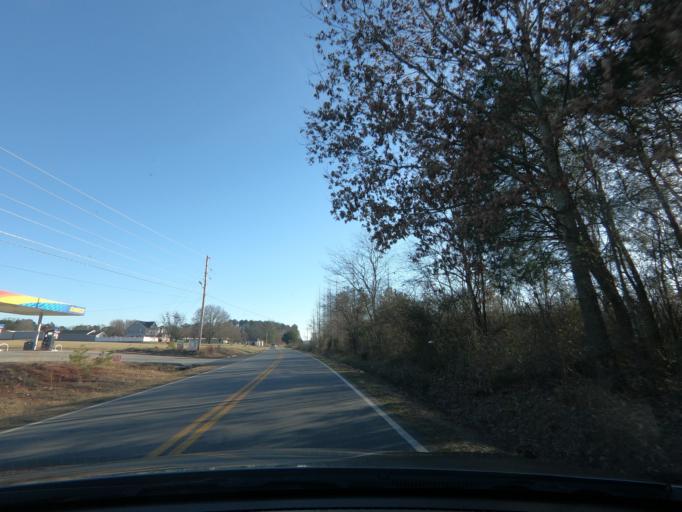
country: US
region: Georgia
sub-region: Gordon County
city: Calhoun
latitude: 34.4521
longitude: -84.9147
